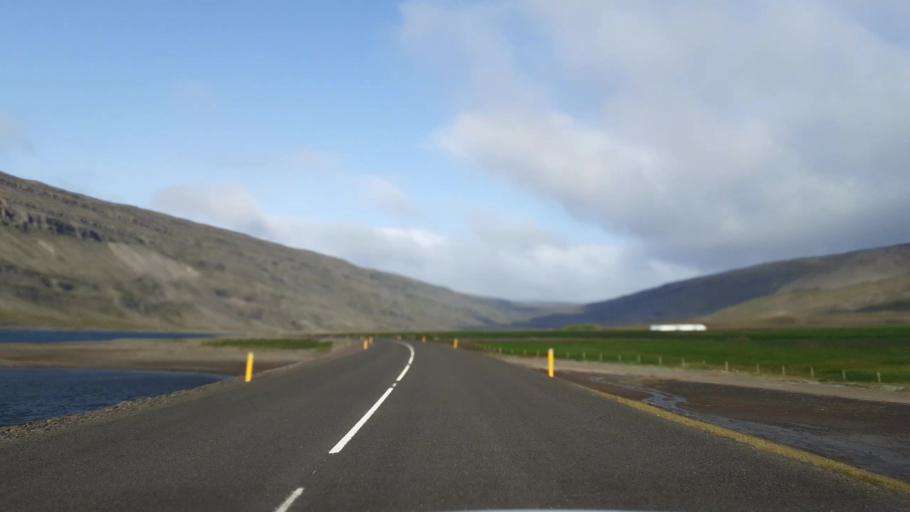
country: IS
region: East
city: Reydarfjoerdur
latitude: 64.7888
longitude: -14.4510
